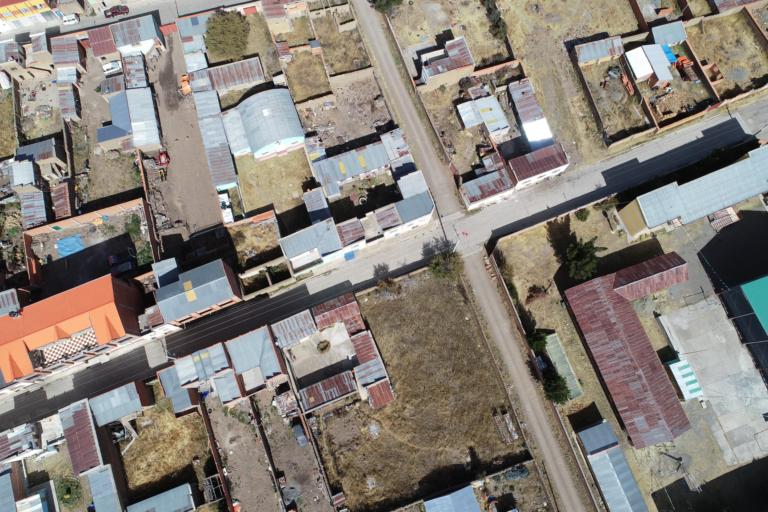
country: BO
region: La Paz
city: Achacachi
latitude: -15.8963
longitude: -68.9069
